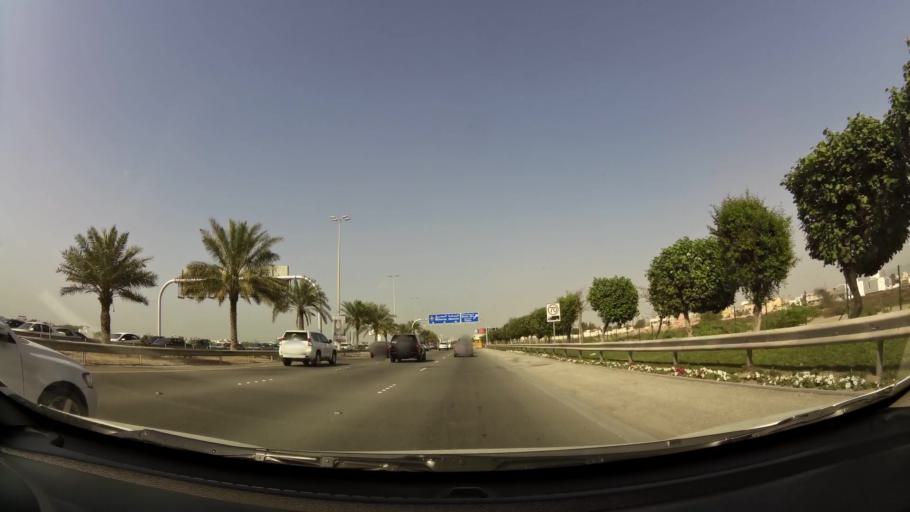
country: BH
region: Manama
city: Jidd Hafs
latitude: 26.2045
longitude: 50.5142
